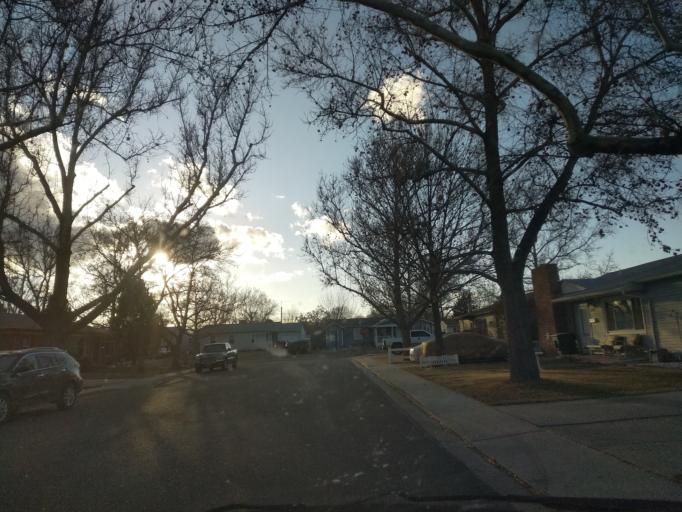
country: US
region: Colorado
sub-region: Mesa County
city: Grand Junction
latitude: 39.0710
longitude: -108.5424
